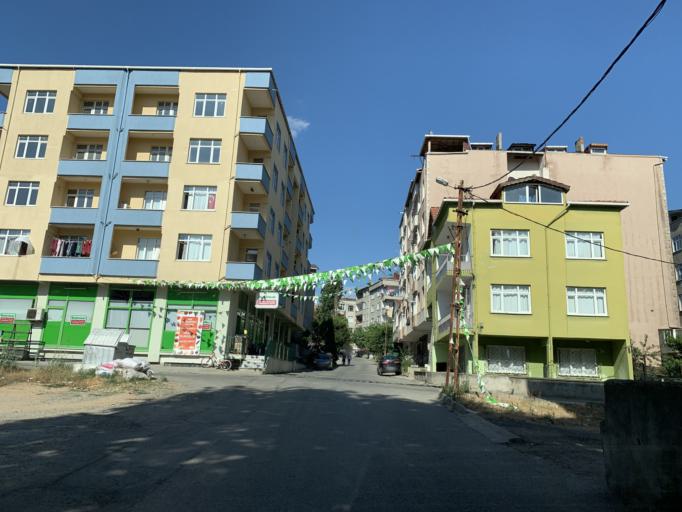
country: TR
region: Istanbul
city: Pendik
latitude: 40.8731
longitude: 29.2781
